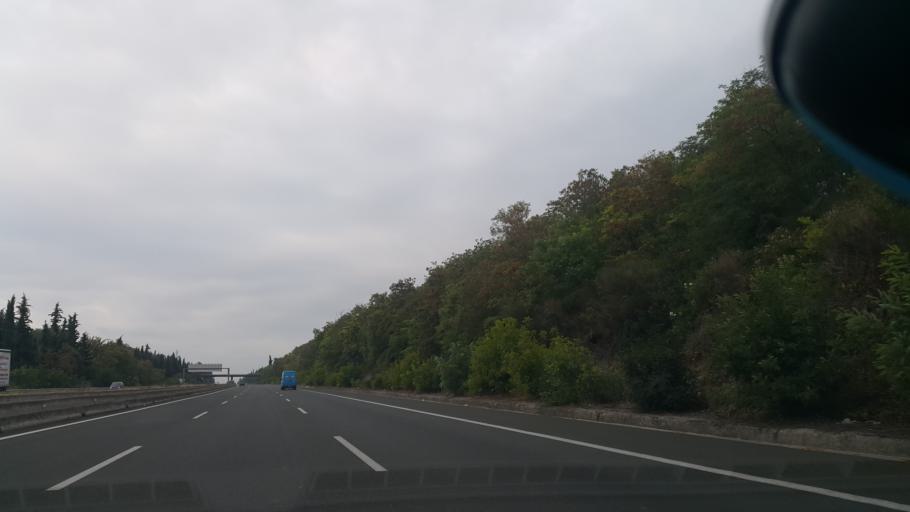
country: GR
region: Central Macedonia
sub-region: Nomos Pierias
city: Makrygialos
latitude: 40.4501
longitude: 22.5807
